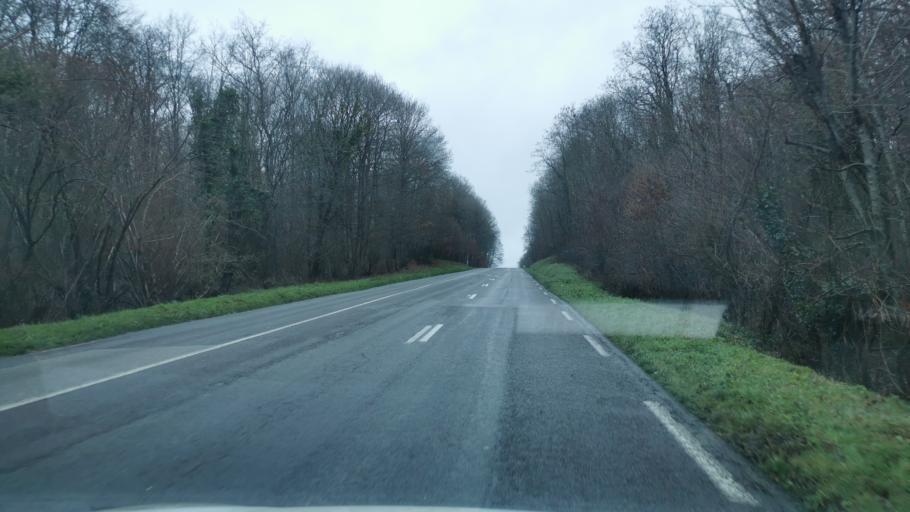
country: FR
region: Haute-Normandie
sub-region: Departement de l'Eure
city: Normanville
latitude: 49.0748
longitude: 1.1771
